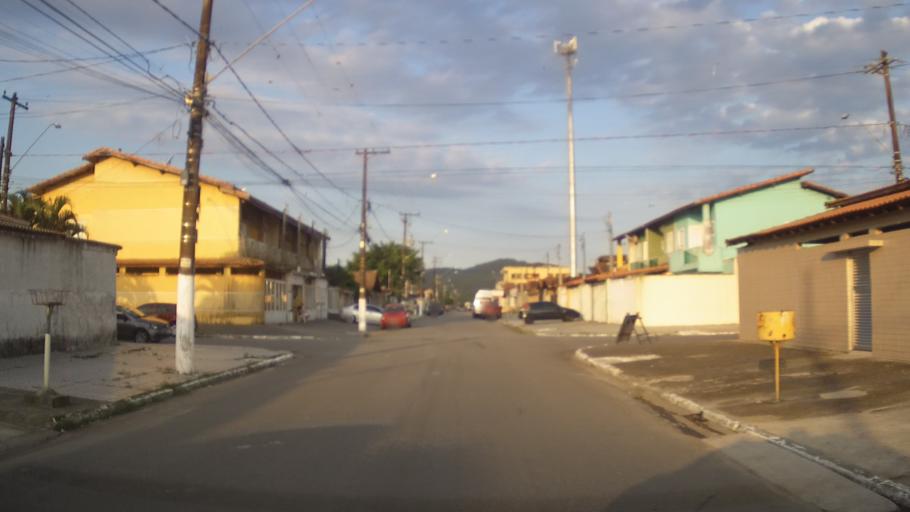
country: BR
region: Sao Paulo
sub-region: Praia Grande
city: Praia Grande
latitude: -23.9972
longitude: -46.4238
